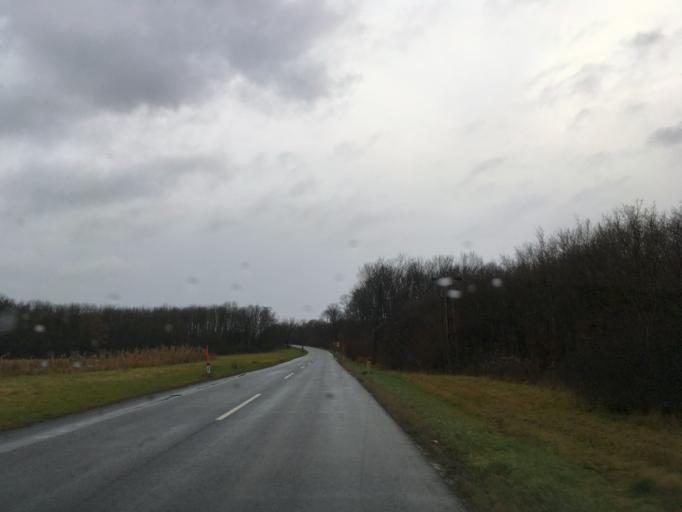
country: AT
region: Lower Austria
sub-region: Politischer Bezirk Wien-Umgebung
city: Rauchenwarth
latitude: 48.0800
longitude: 16.5352
